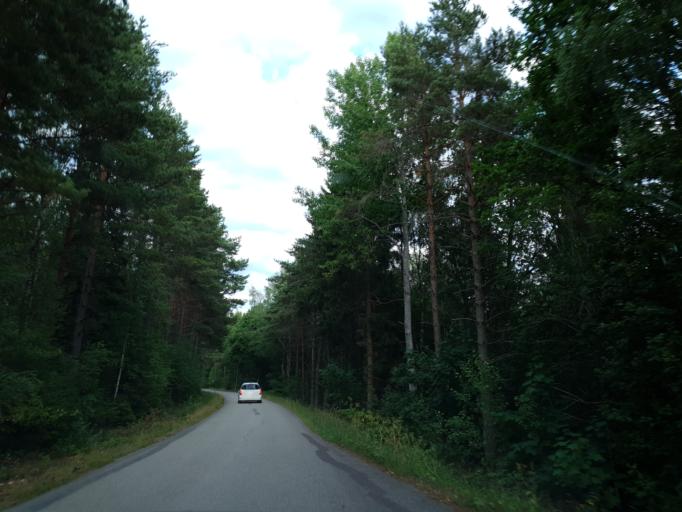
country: SE
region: Kalmar
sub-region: Emmaboda Kommun
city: Emmaboda
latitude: 56.6229
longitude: 15.6480
